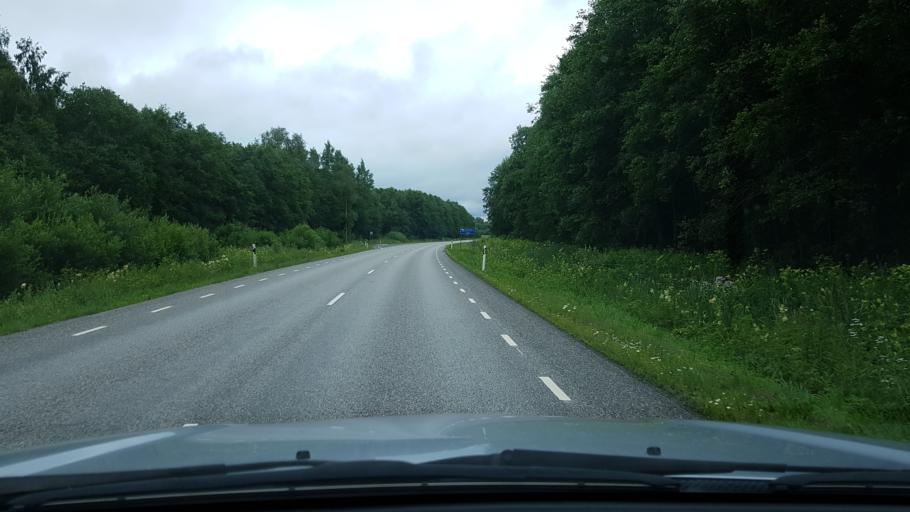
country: EE
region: Ida-Virumaa
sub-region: Narva-Joesuu linn
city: Narva-Joesuu
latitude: 59.3458
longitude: 27.9331
